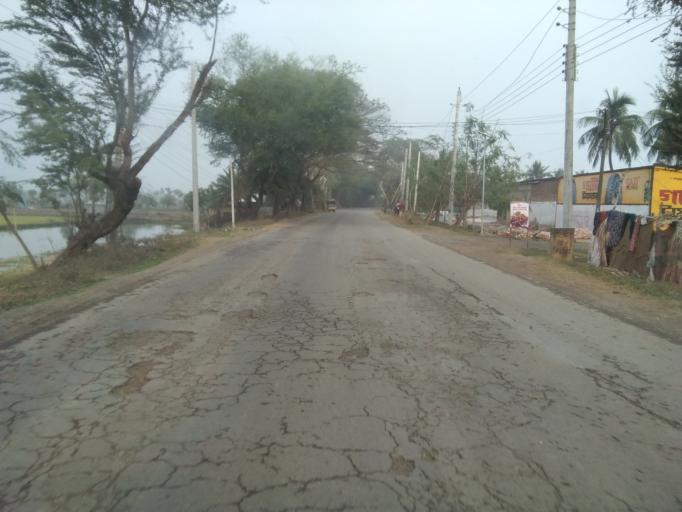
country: BD
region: Khulna
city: Satkhira
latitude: 22.6897
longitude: 89.0352
